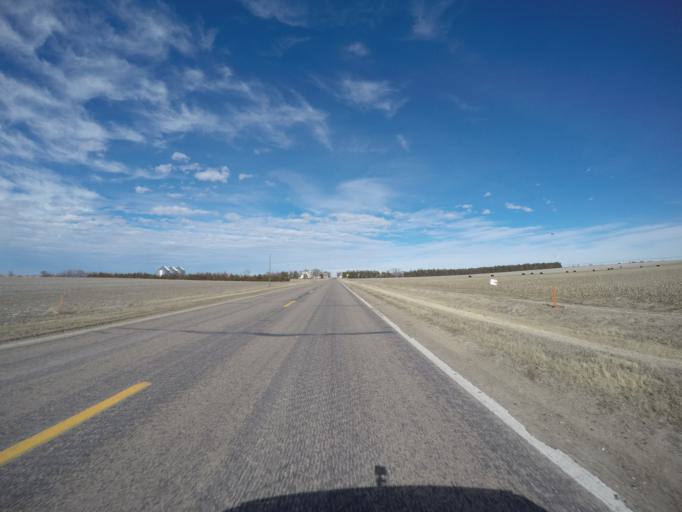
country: US
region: Nebraska
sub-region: Franklin County
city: Franklin
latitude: 40.1996
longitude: -98.9525
